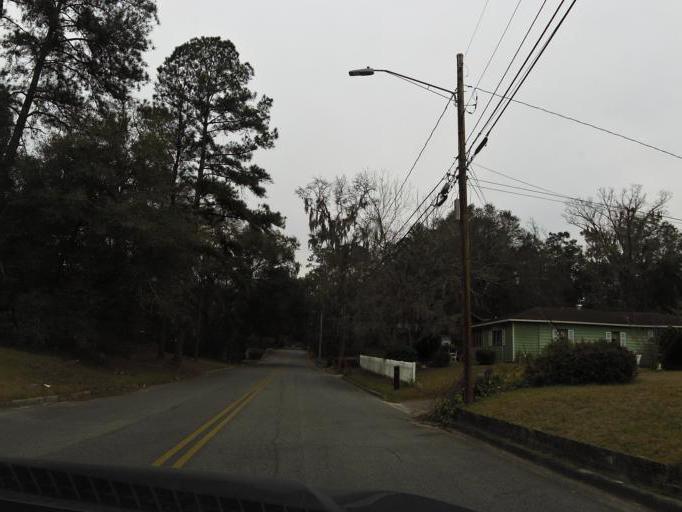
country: US
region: Georgia
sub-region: Thomas County
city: Thomasville
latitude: 30.8224
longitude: -83.9772
